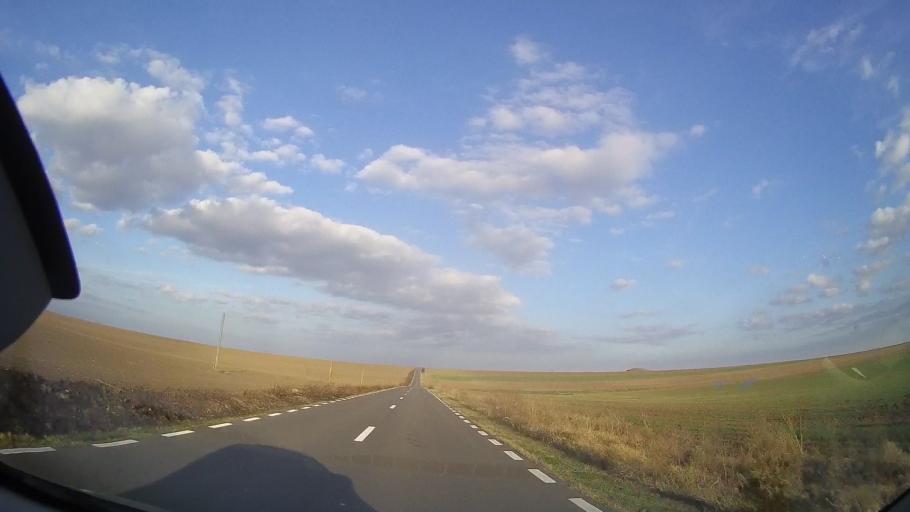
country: RO
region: Constanta
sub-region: Comuna Independenta
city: Independenta
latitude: 43.9406
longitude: 28.0478
